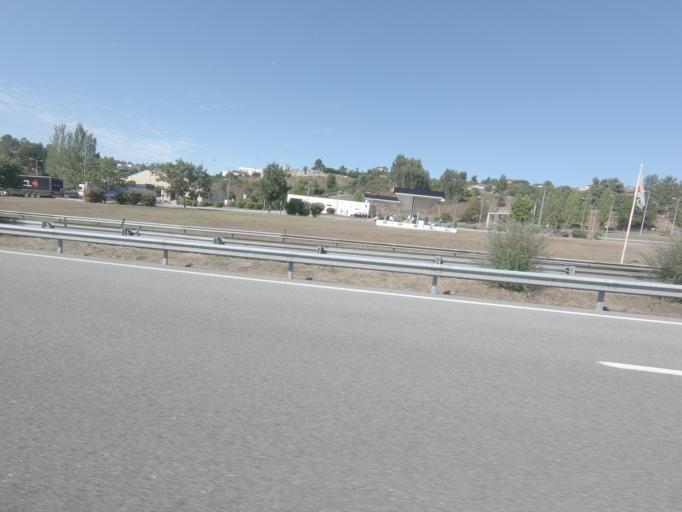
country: PT
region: Porto
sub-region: Marco de Canaveses
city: Marco de Canavezes
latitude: 41.2336
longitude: -8.1780
